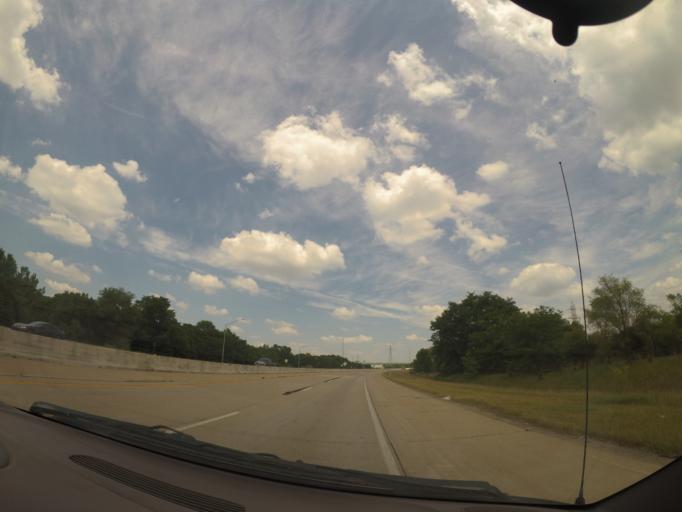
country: US
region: Indiana
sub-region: Elkhart County
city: Dunlap
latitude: 41.6639
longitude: -85.8990
